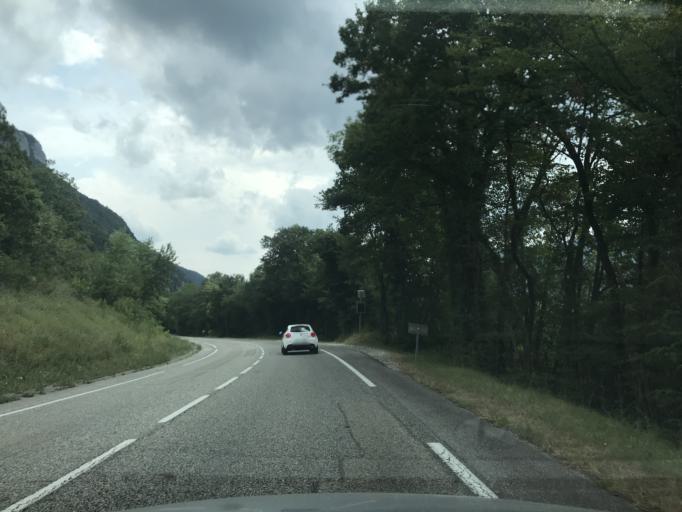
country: FR
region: Rhone-Alpes
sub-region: Departement de la Savoie
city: Chatillon
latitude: 45.7871
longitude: 5.8609
